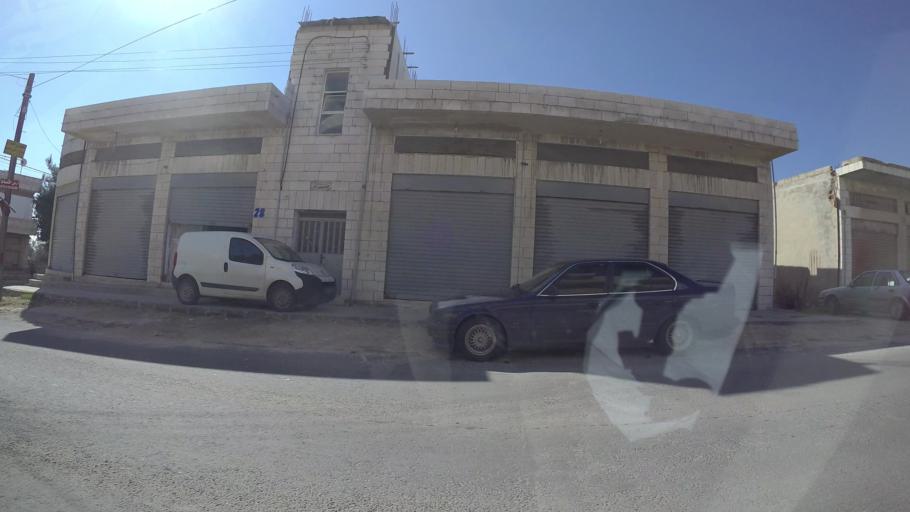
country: JO
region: Amman
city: Al Bunayyat ash Shamaliyah
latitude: 31.9049
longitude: 35.8990
